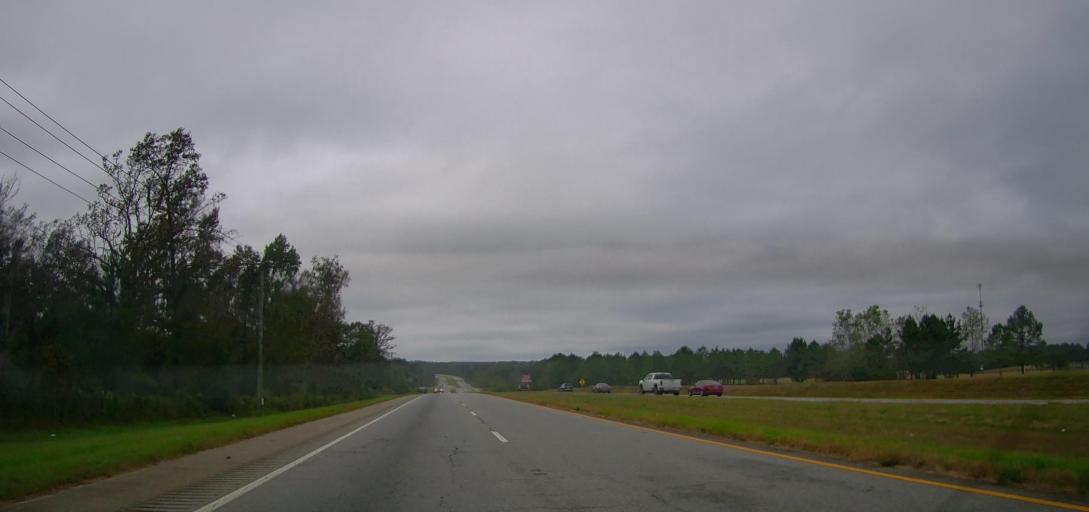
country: US
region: Georgia
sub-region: Thomas County
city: Thomasville
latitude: 30.8748
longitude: -83.9710
